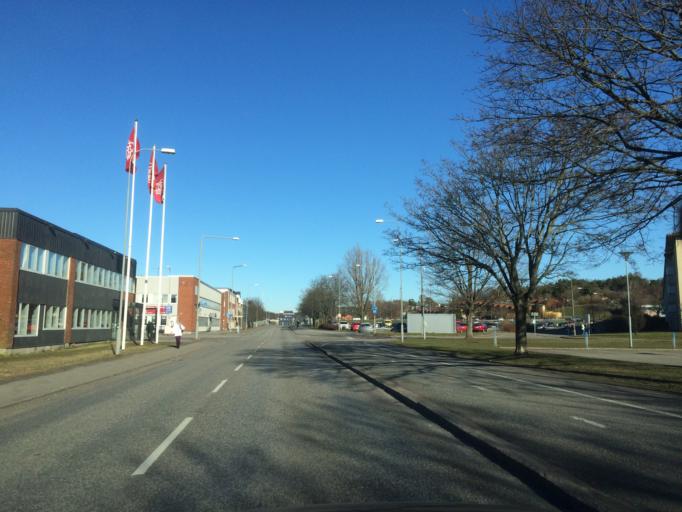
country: SE
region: Vaestra Goetaland
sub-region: Goteborg
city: Majorna
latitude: 57.6560
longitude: 11.9017
